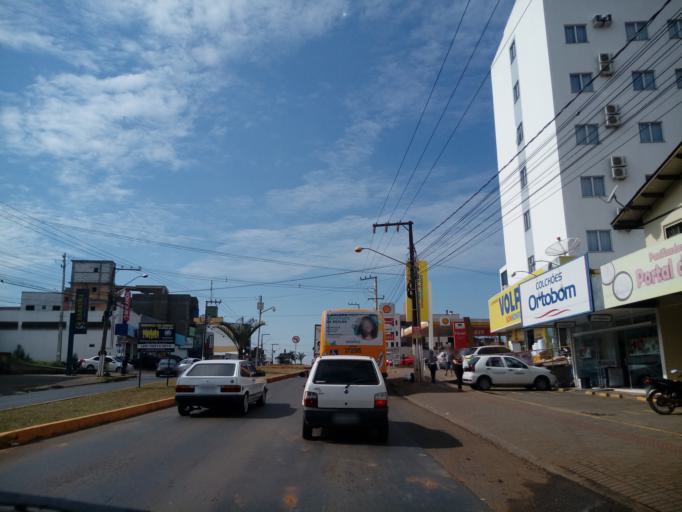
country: BR
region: Santa Catarina
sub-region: Chapeco
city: Chapeco
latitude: -27.0954
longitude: -52.6757
